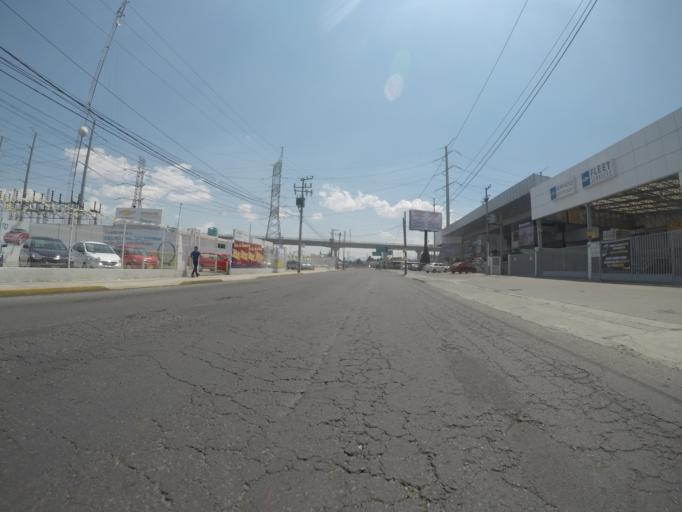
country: MX
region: Mexico
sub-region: Metepec
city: San Jorge Pueblo Nuevo
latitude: 19.2741
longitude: -99.6318
